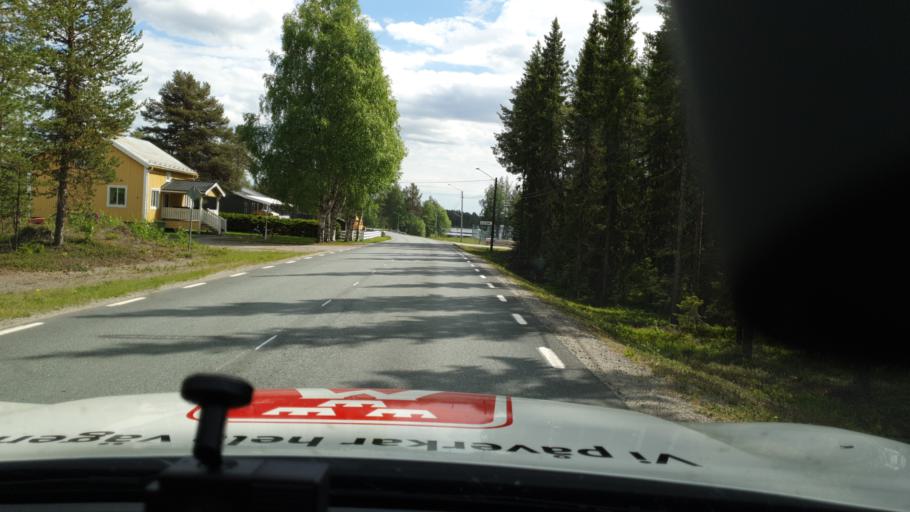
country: SE
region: Vaesterbotten
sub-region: Sorsele Kommun
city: Sorsele
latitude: 65.3453
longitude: 17.5779
